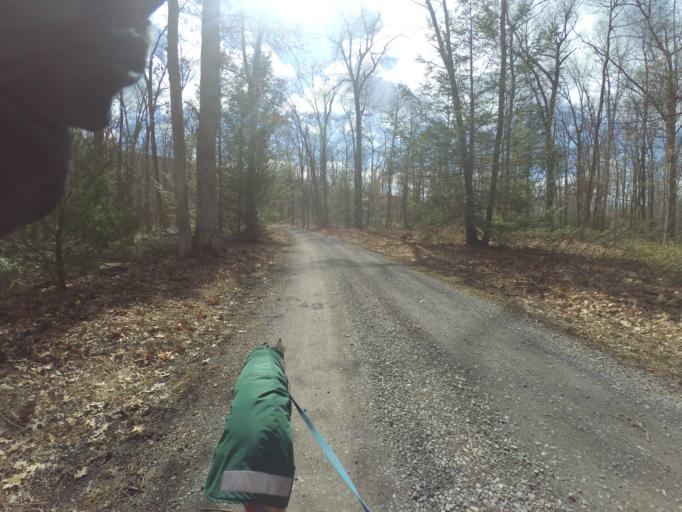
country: US
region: Pennsylvania
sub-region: Centre County
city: Boalsburg
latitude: 40.7575
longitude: -77.7089
